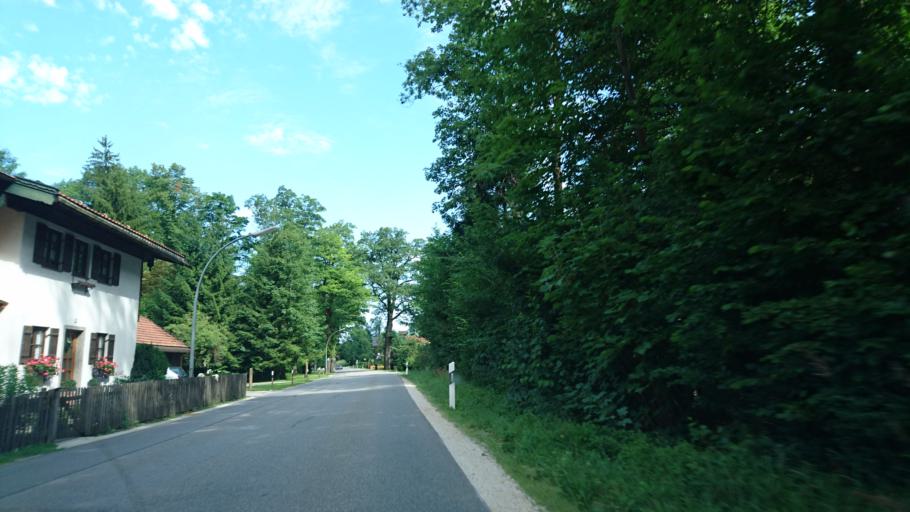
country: DE
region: Bavaria
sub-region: Upper Bavaria
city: Ruhpolding
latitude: 47.7598
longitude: 12.6582
